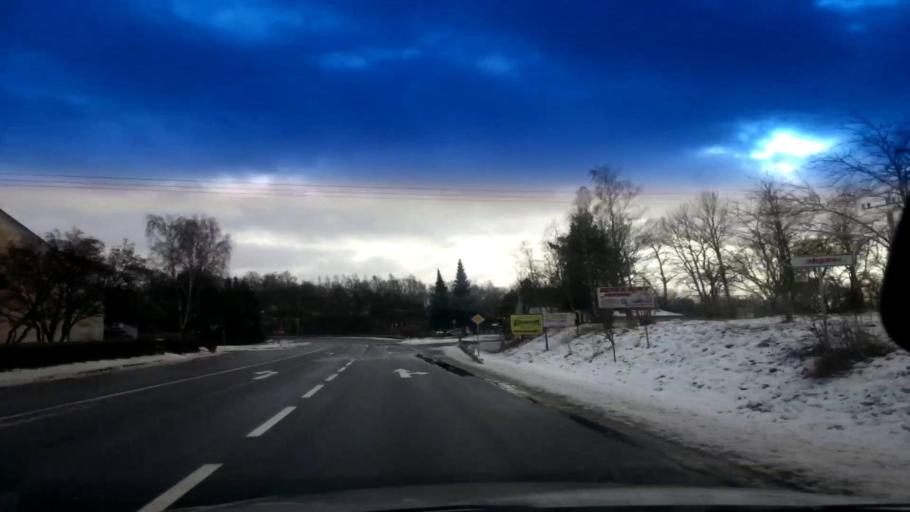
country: CZ
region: Karlovarsky
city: Hazlov
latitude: 50.1571
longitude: 12.2719
